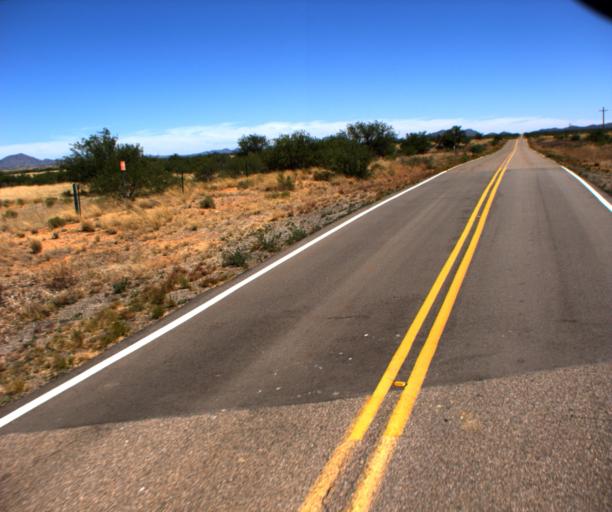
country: US
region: Arizona
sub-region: Pima County
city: Sells
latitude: 31.5519
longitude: -111.5396
